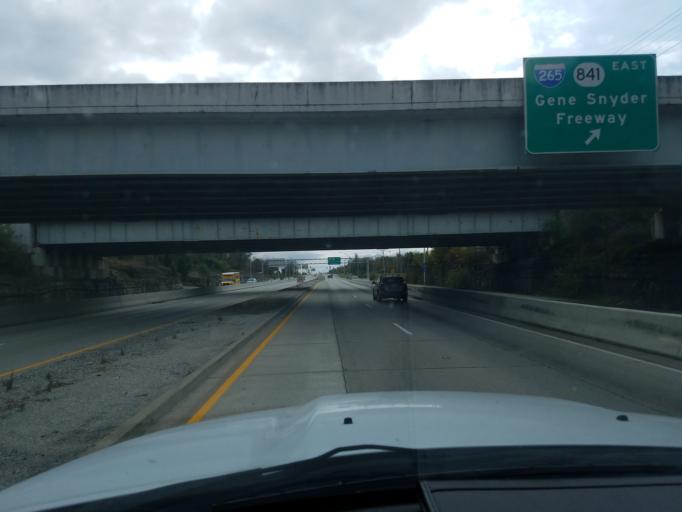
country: US
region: Kentucky
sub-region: Jefferson County
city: Fern Creek
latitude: 38.1421
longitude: -85.5835
